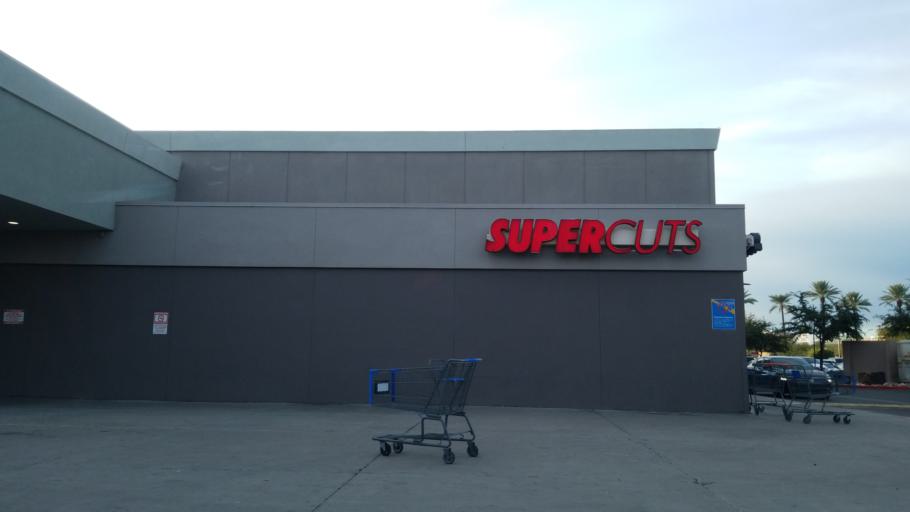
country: US
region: Arizona
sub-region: Maricopa County
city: Phoenix
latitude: 33.5227
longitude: -112.0938
